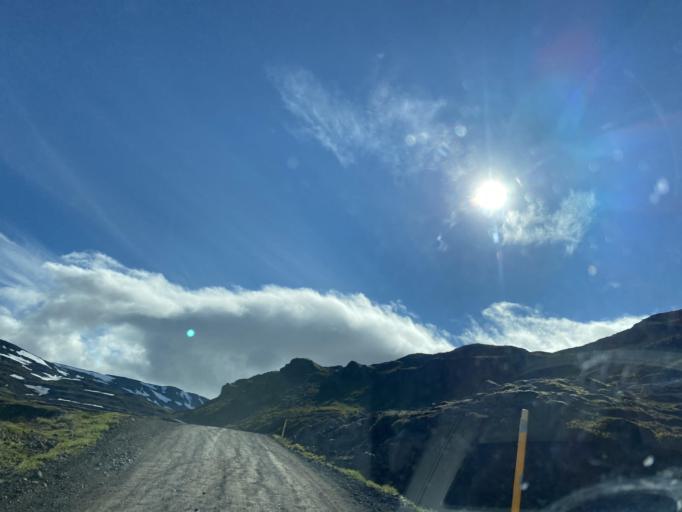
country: IS
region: East
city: Eskifjoerdur
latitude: 65.1774
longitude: -14.1084
